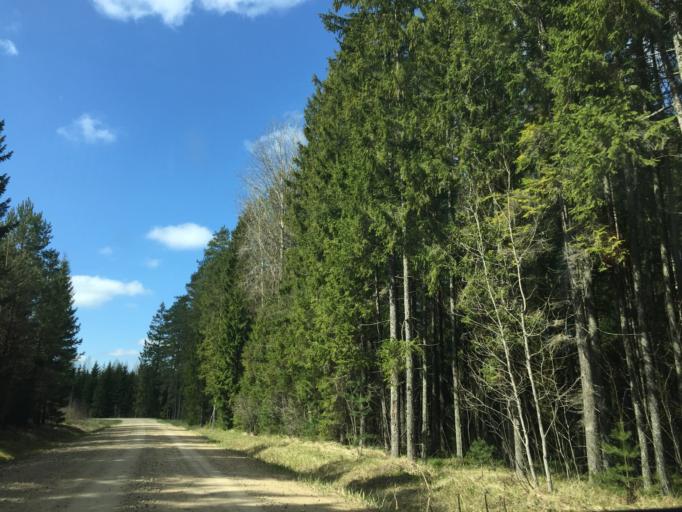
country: EE
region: Valgamaa
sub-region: Valga linn
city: Valga
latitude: 57.5947
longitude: 26.0686
